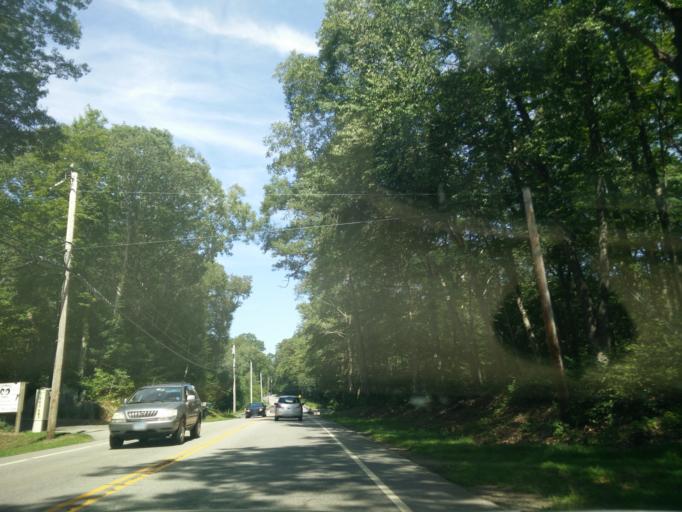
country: US
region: Connecticut
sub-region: Middlesex County
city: Clinton
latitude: 41.3174
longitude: -72.5418
